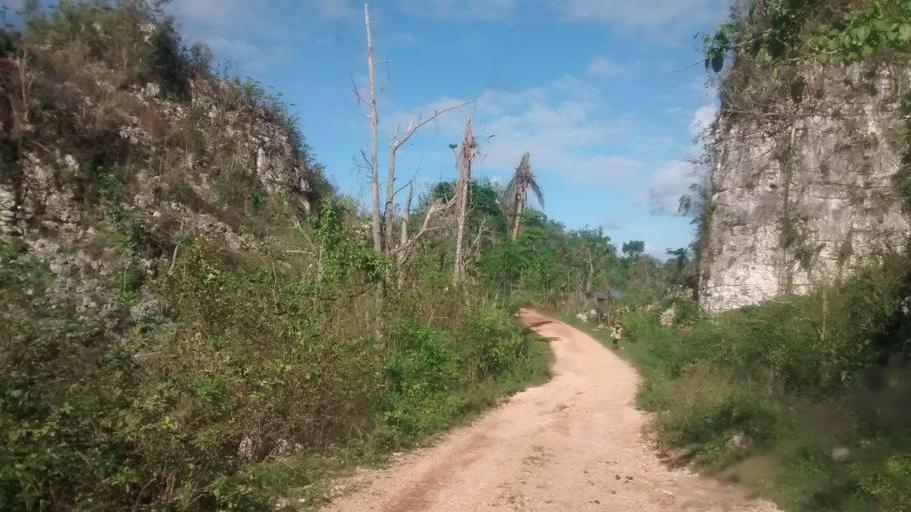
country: HT
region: Grandans
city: Corail
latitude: 18.5311
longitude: -73.8449
